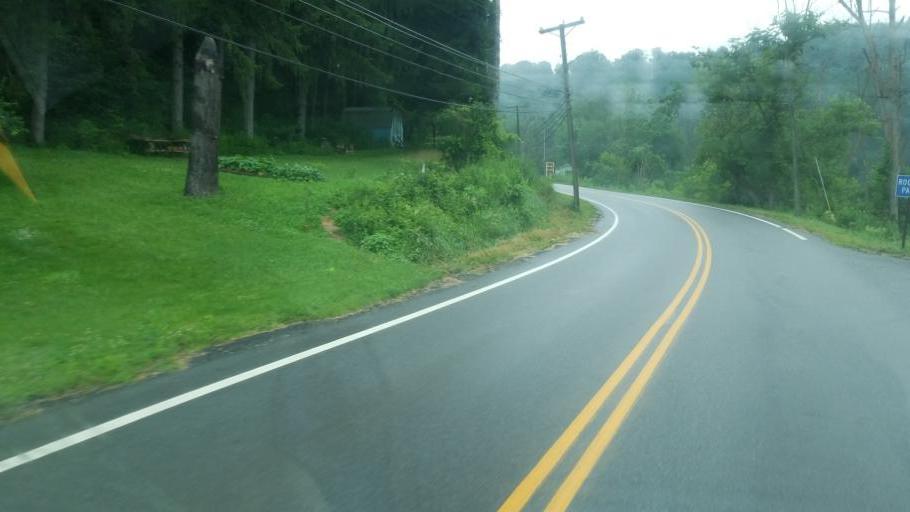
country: US
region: Ohio
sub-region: Columbiana County
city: Salineville
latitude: 40.4781
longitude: -80.9199
